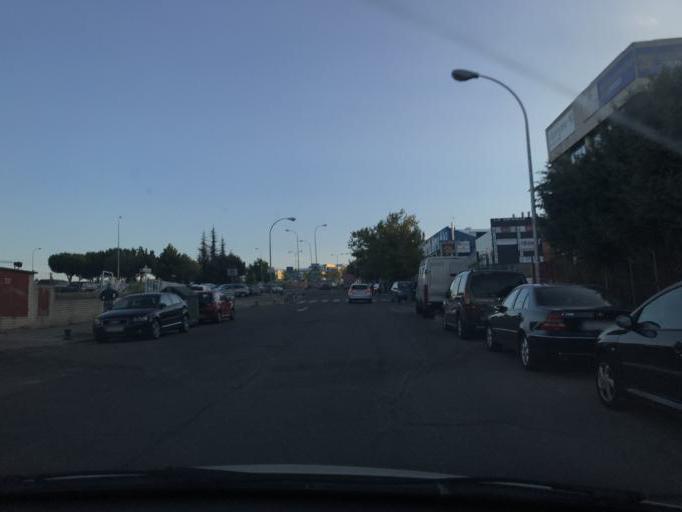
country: ES
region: Madrid
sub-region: Provincia de Madrid
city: Alcobendas
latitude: 40.5349
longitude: -3.6568
